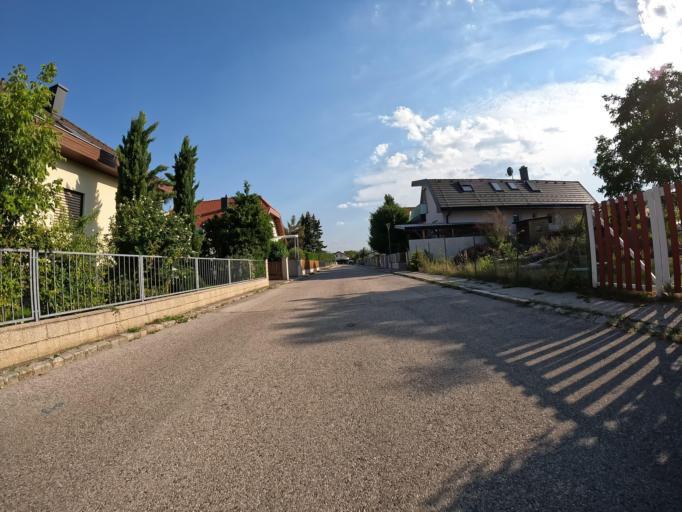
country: AT
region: Lower Austria
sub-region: Politischer Bezirk Modling
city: Guntramsdorf
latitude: 48.0413
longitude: 16.3125
